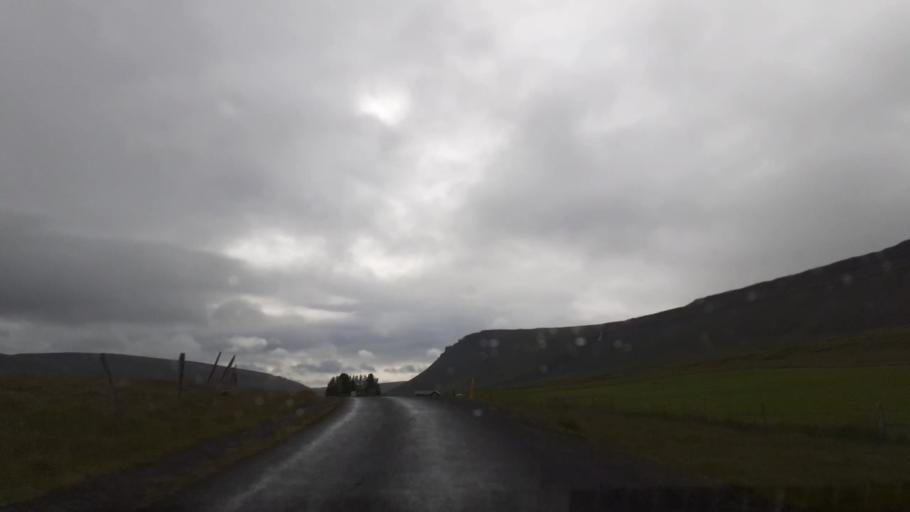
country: IS
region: East
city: Egilsstadir
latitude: 65.6182
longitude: -15.0926
